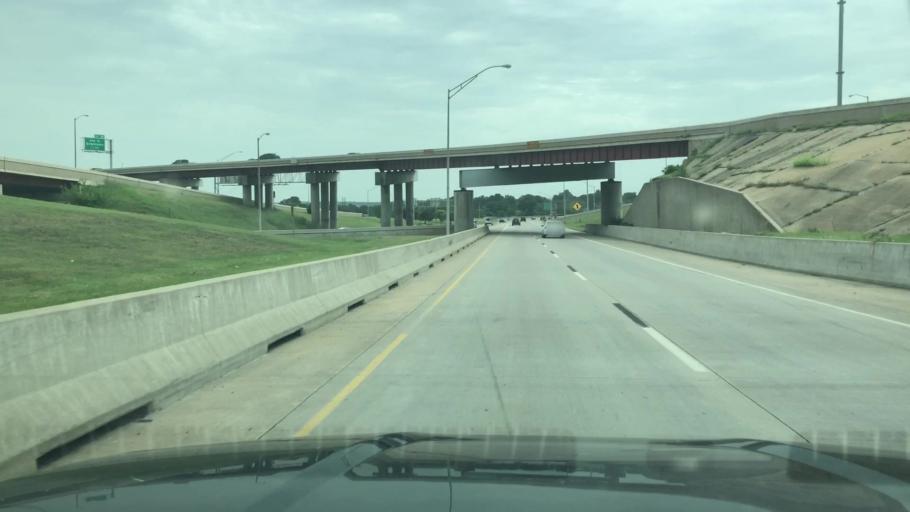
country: US
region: Oklahoma
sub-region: Tulsa County
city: Tulsa
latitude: 36.1596
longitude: -96.0012
